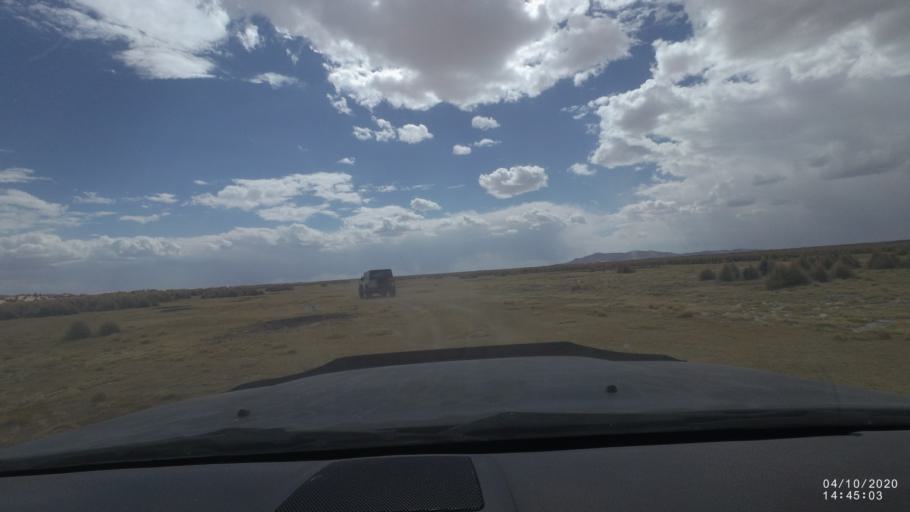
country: BO
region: Oruro
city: Poopo
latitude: -18.6864
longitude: -67.4970
